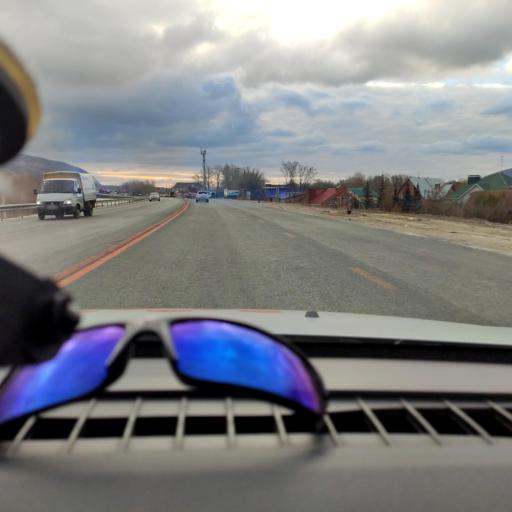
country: RU
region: Samara
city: Volzhskiy
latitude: 53.4188
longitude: 50.1281
